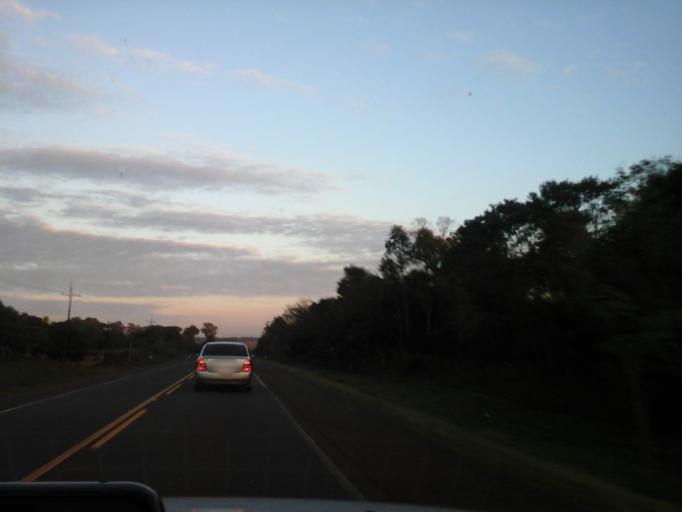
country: PY
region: Itapua
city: General Delgado
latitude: -27.0846
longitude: -56.5482
